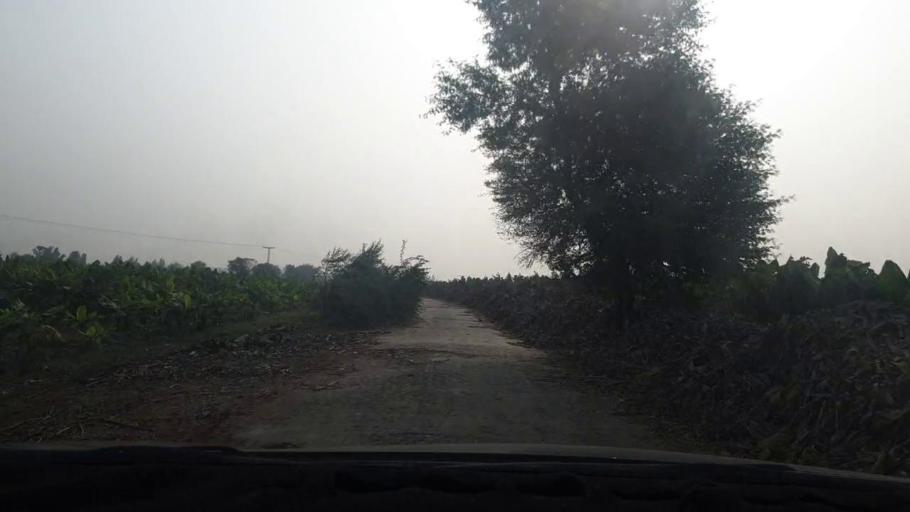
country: PK
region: Sindh
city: Matiari
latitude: 25.5932
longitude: 68.5421
